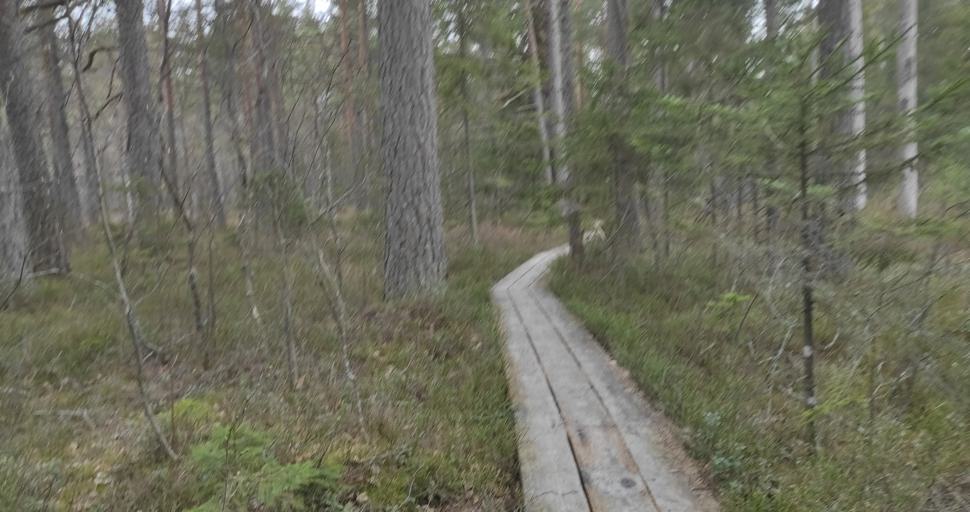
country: LV
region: Dundaga
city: Dundaga
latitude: 57.3442
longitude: 22.1513
